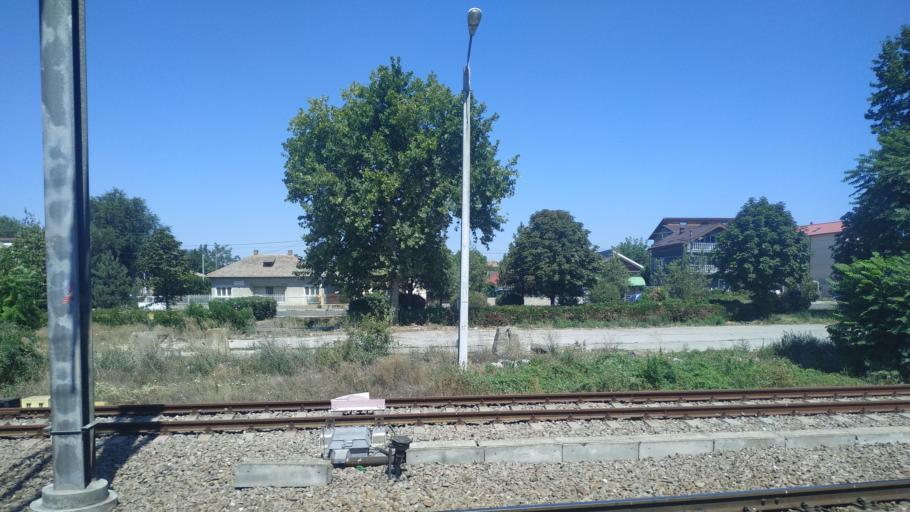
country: RO
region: Constanta
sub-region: Oras Murfatlar
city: Murfatlar
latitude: 44.1719
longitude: 28.4151
